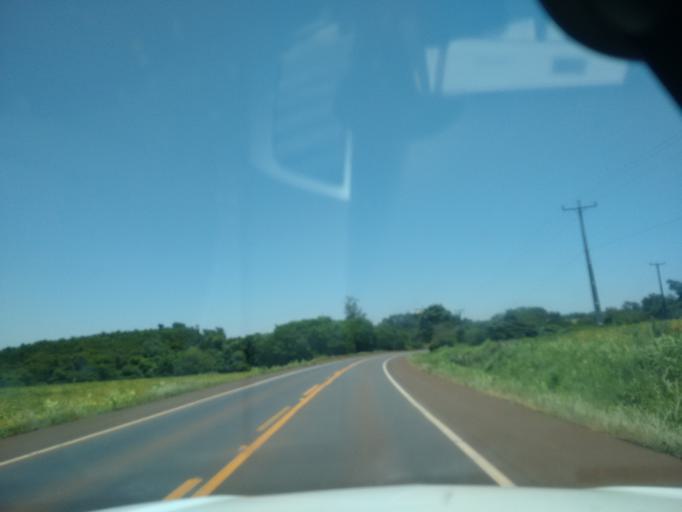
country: BR
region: Parana
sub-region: Marechal Candido Rondon
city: Marechal Candido Rondon
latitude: -24.4692
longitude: -54.1494
